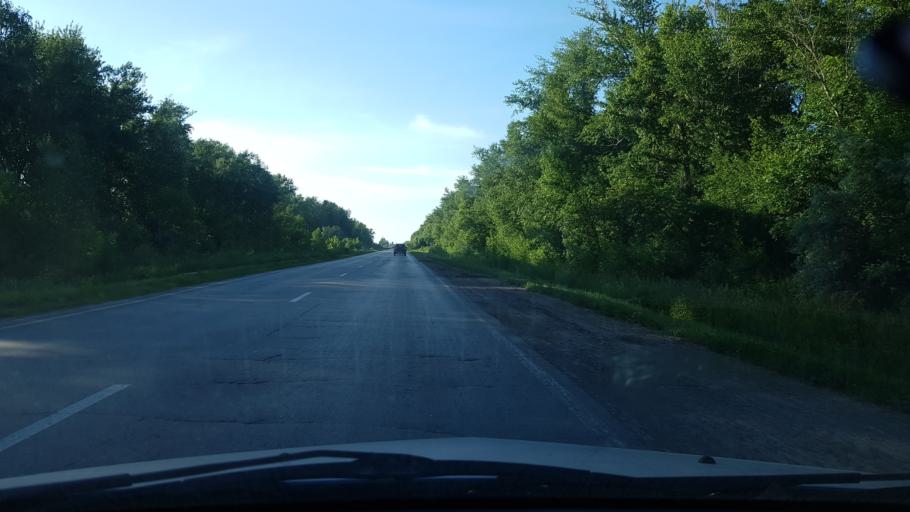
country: RU
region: Samara
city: Tol'yatti
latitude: 53.6247
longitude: 49.3070
